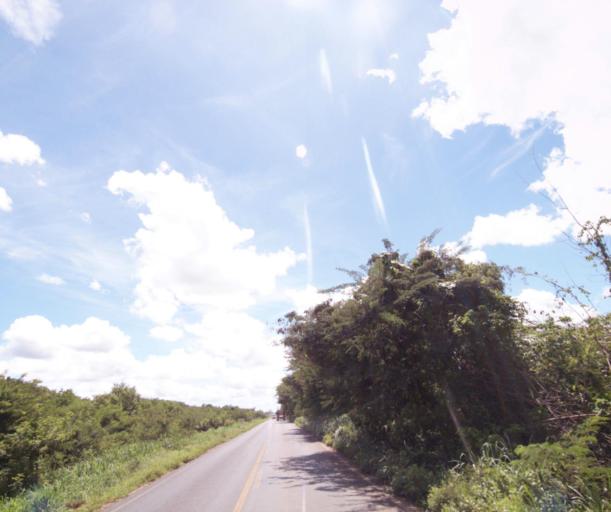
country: BR
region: Bahia
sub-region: Bom Jesus Da Lapa
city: Bom Jesus da Lapa
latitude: -13.2634
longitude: -43.5536
